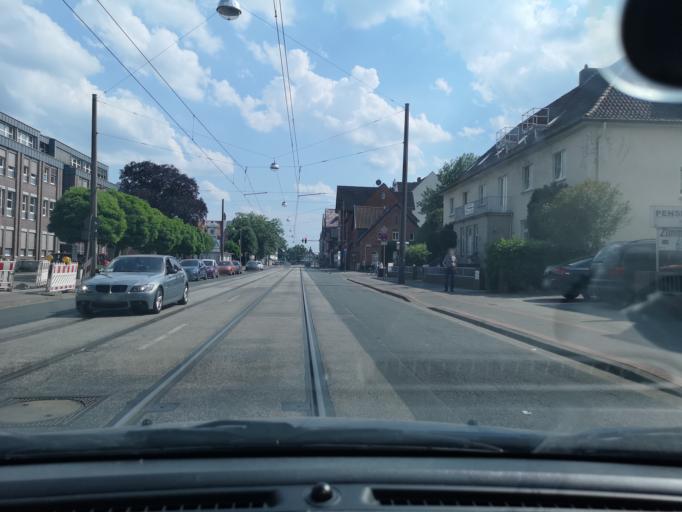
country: DE
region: Lower Saxony
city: Langenhagen
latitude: 52.4095
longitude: 9.7994
